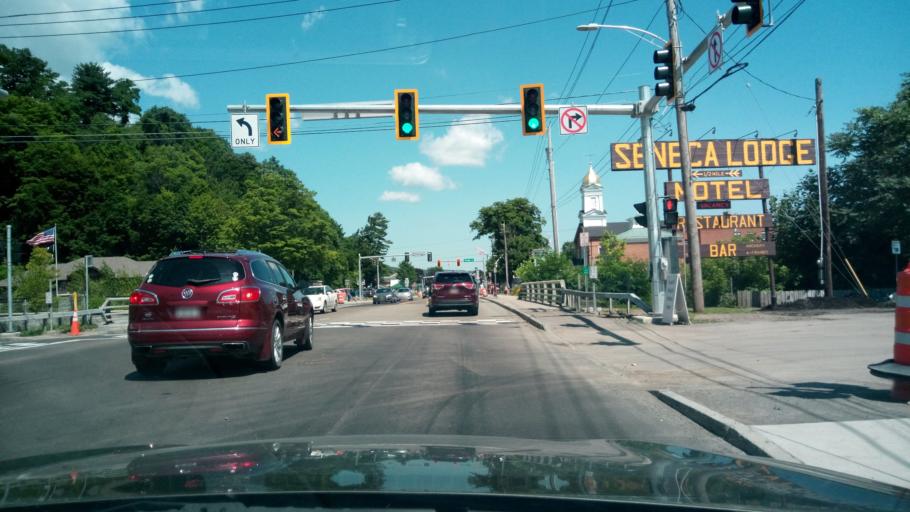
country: US
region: New York
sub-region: Schuyler County
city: Watkins Glen
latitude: 42.3754
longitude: -76.8707
